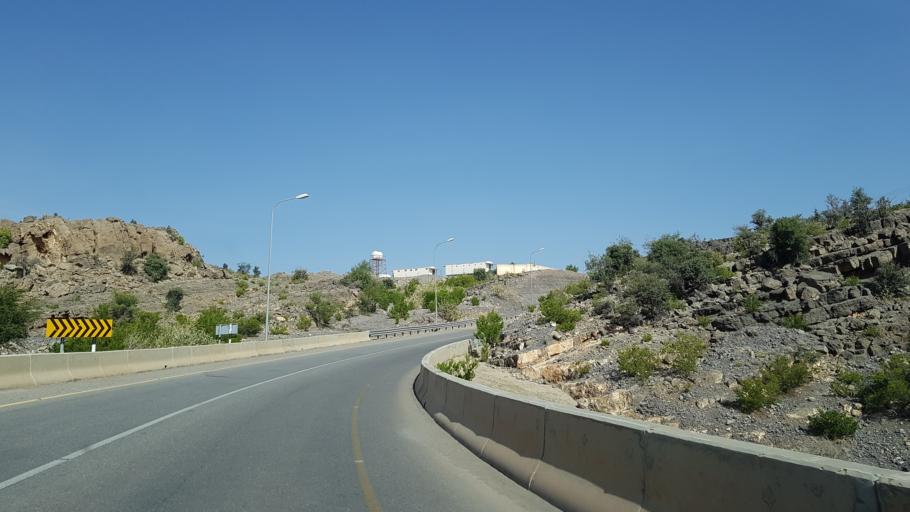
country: OM
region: Muhafazat ad Dakhiliyah
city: Izki
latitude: 23.0909
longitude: 57.6911
